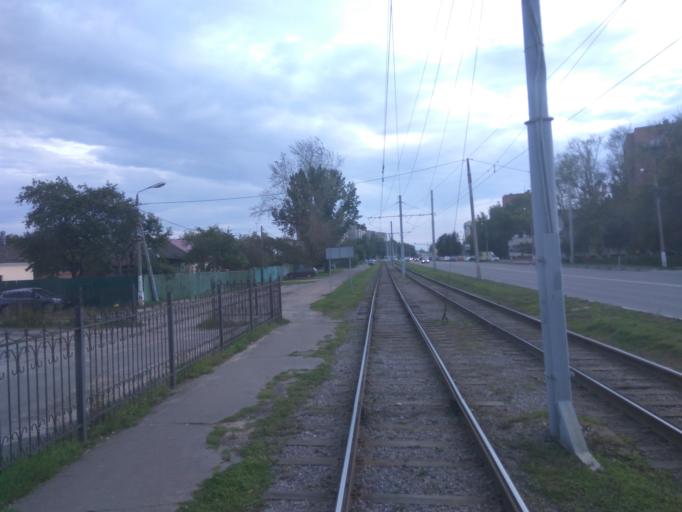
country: RU
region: Moskovskaya
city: Kolomna
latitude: 55.0800
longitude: 38.7624
